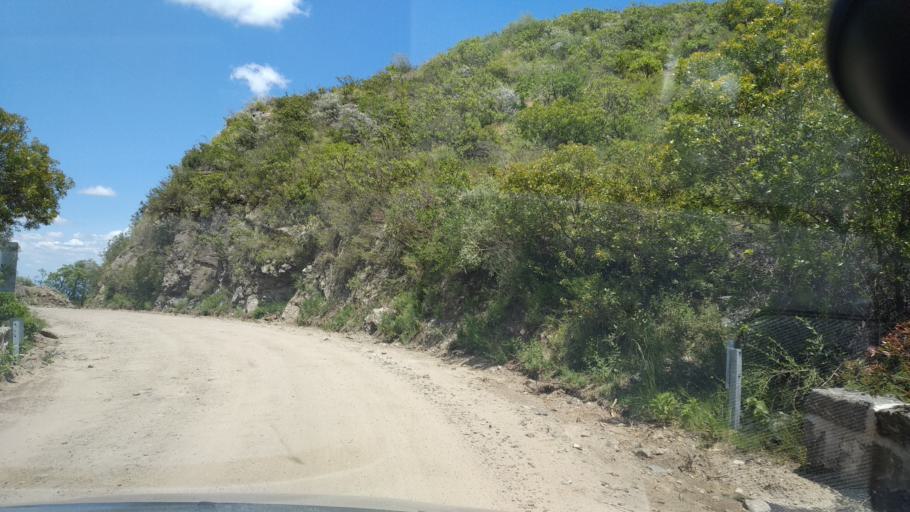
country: AR
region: Cordoba
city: Salsacate
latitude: -31.3766
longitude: -65.4013
